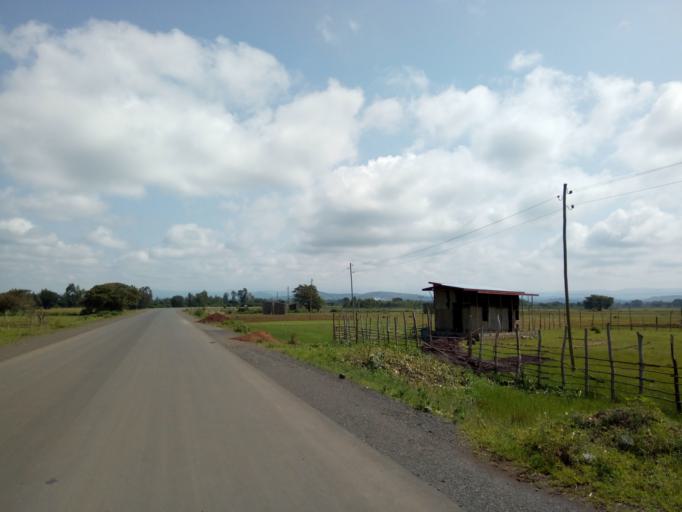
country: ET
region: Oromiya
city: Waliso
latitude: 8.5596
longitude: 37.9484
